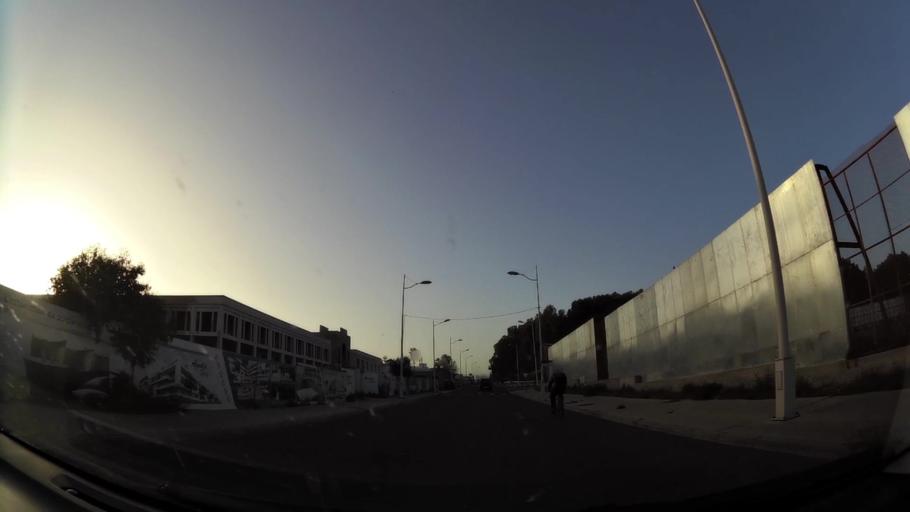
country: MA
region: Souss-Massa-Draa
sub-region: Agadir-Ida-ou-Tnan
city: Agadir
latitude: 30.4057
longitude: -9.5936
